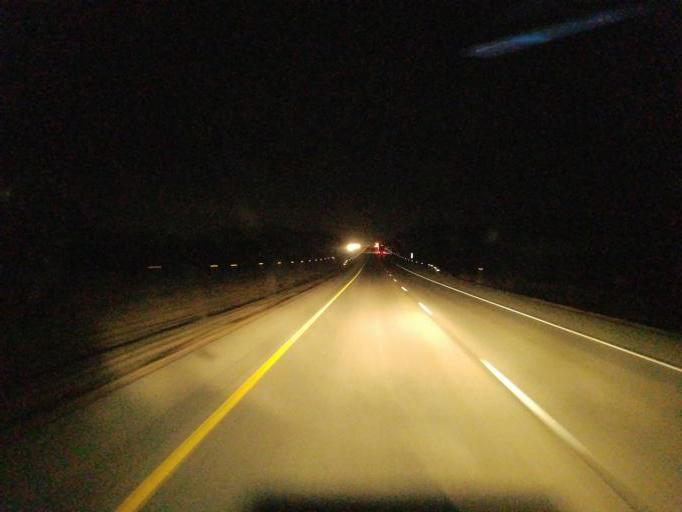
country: US
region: Iowa
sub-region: Madison County
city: Earlham
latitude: 41.5176
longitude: -94.1450
